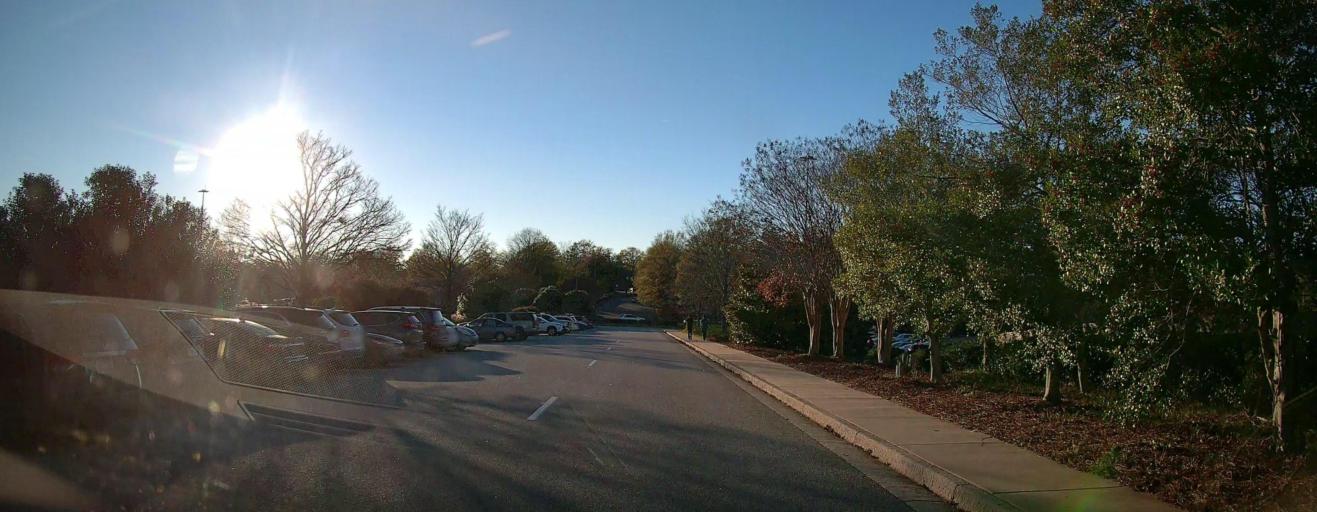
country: US
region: Georgia
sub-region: Gwinnett County
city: Buford
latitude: 34.0633
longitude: -83.9867
